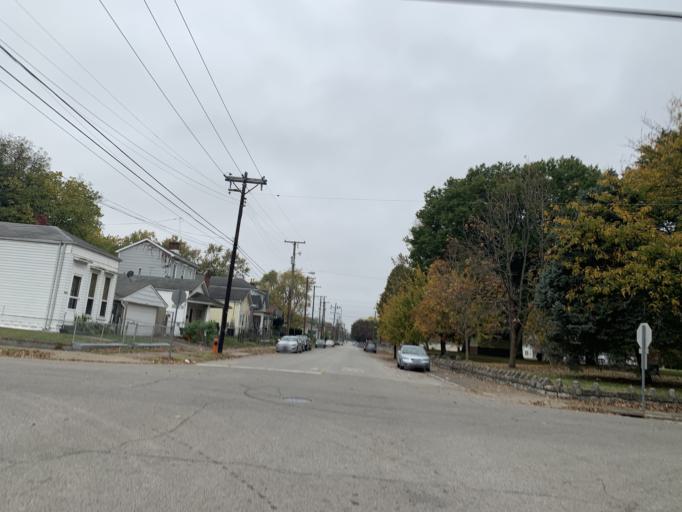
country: US
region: Kentucky
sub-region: Jefferson County
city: Louisville
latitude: 38.2607
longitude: -85.7810
